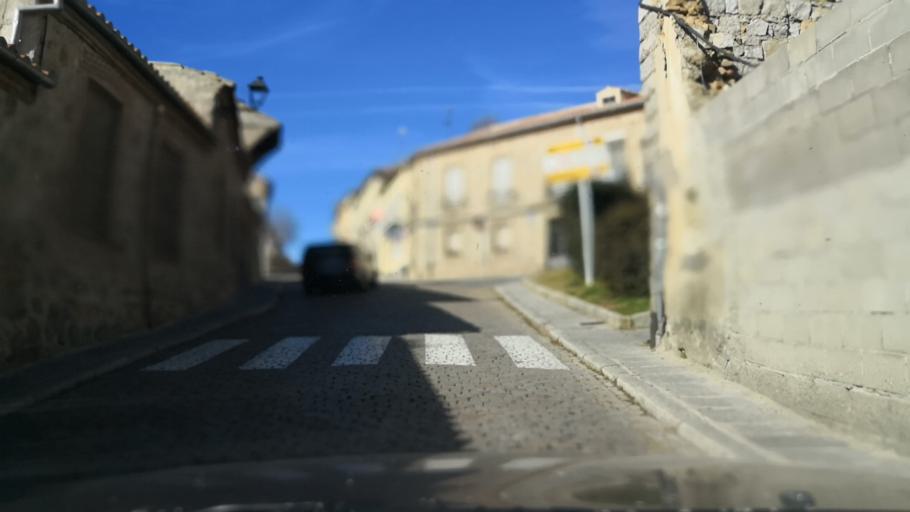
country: ES
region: Castille and Leon
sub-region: Provincia de Avila
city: Avila
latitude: 40.6535
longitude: -4.6987
